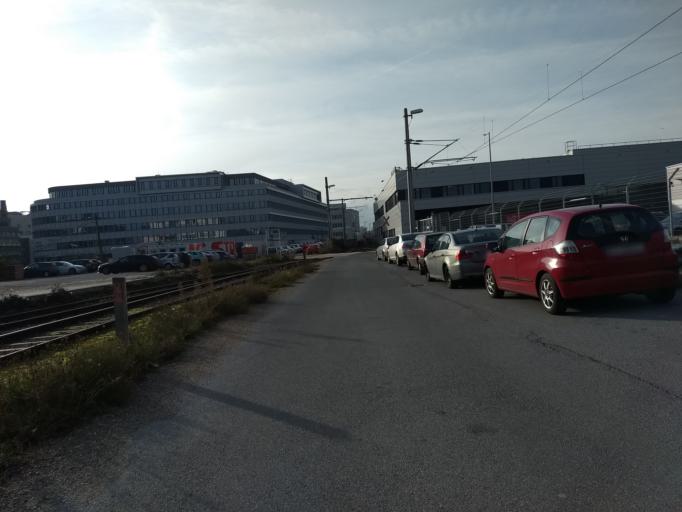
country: AT
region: Vienna
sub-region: Wien Stadt
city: Vienna
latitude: 48.2499
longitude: 16.3677
